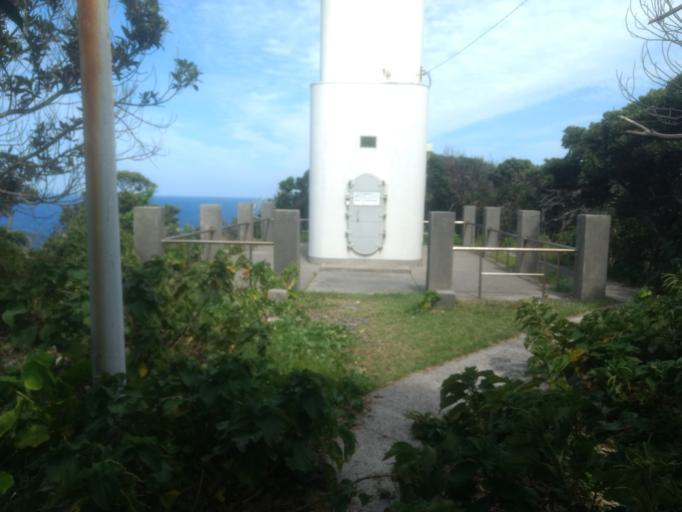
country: JP
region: Kagoshima
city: Nishinoomote
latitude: 30.4687
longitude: 130.4977
